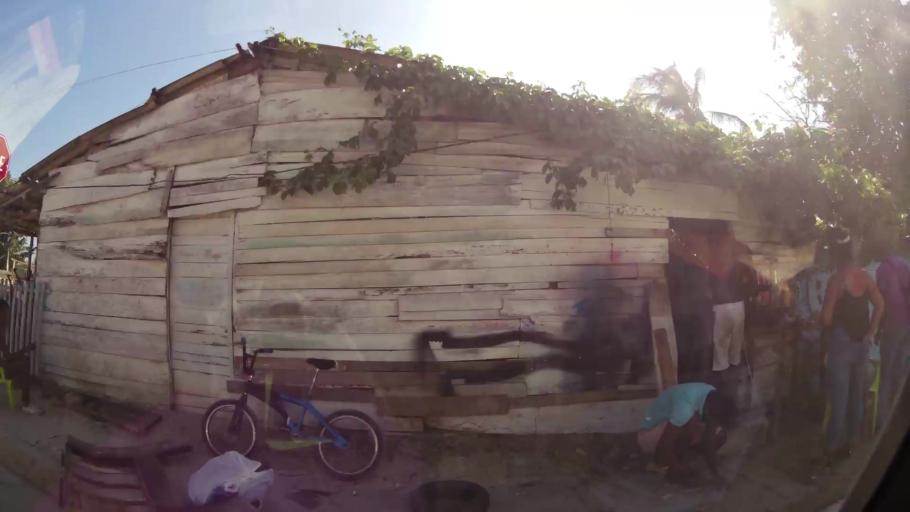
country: CO
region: Bolivar
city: Cartagena
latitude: 10.4133
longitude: -75.5088
